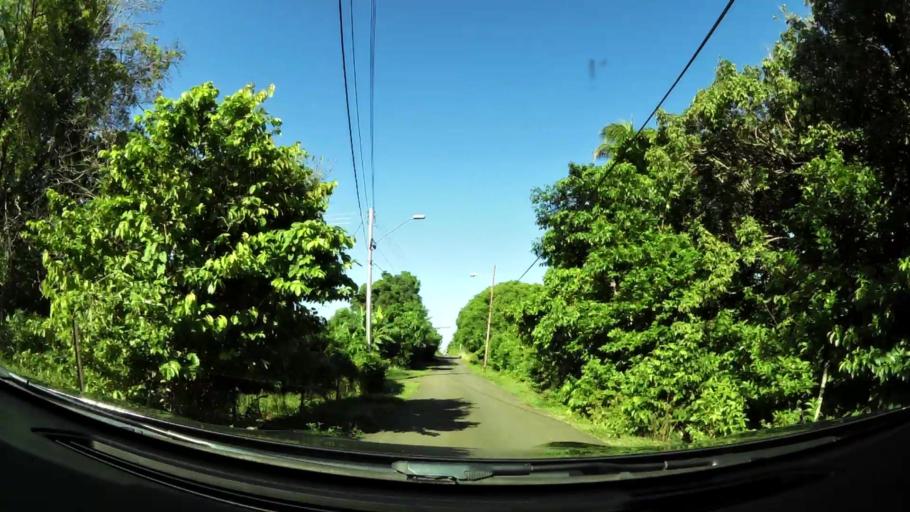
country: TT
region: Tobago
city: Scarborough
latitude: 11.1512
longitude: -60.8286
